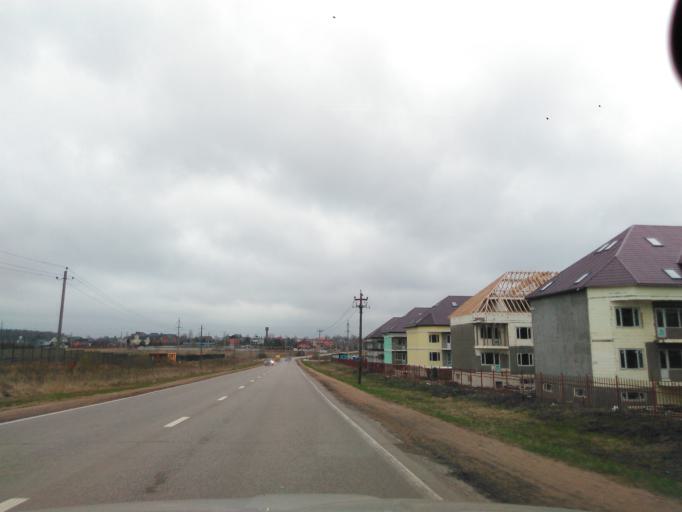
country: RU
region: Moskovskaya
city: Pavlovskaya Sloboda
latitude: 55.8205
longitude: 37.0589
